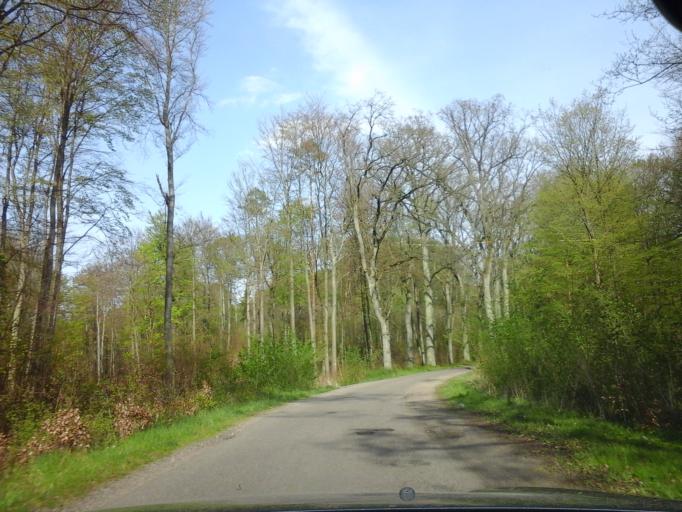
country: PL
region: West Pomeranian Voivodeship
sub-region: Powiat choszczenski
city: Bierzwnik
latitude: 53.0486
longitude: 15.5757
